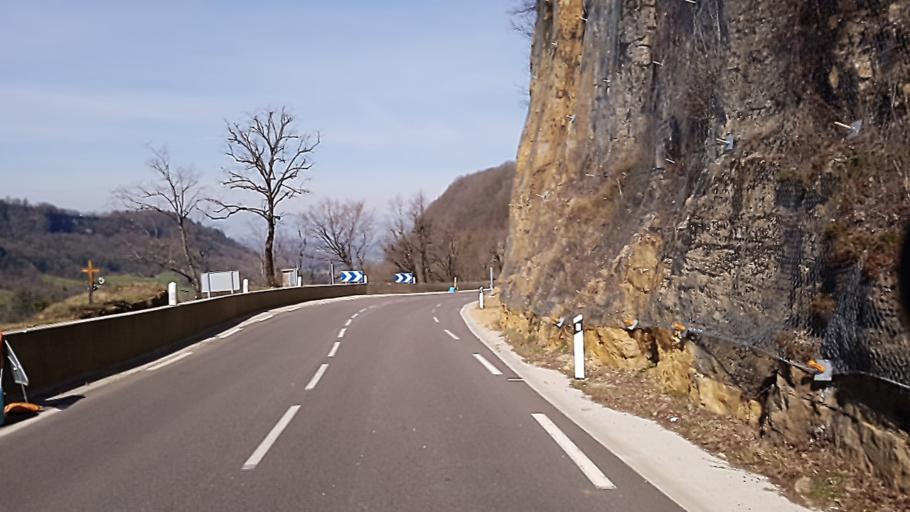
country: FR
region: Franche-Comte
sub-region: Departement du Jura
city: Poligny
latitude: 46.8217
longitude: 5.7350
